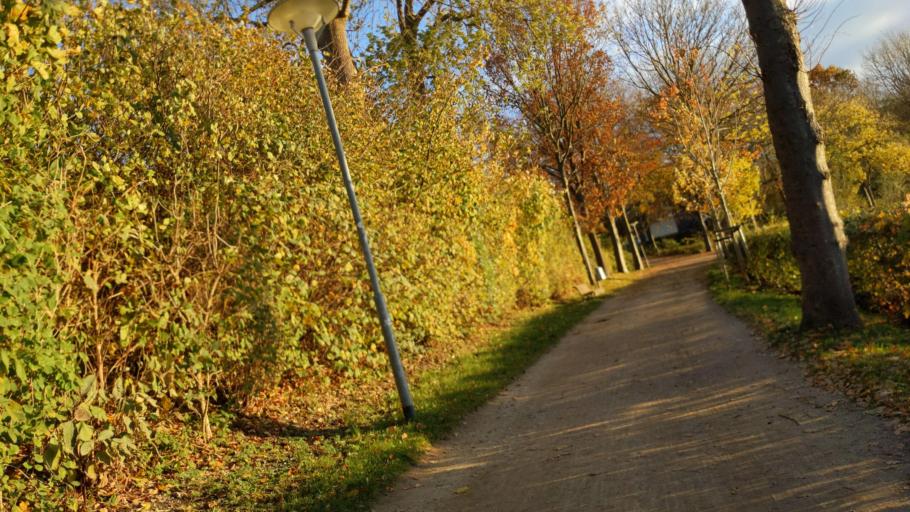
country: DE
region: Schleswig-Holstein
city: Neustadt in Holstein
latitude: 54.0954
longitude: 10.8155
